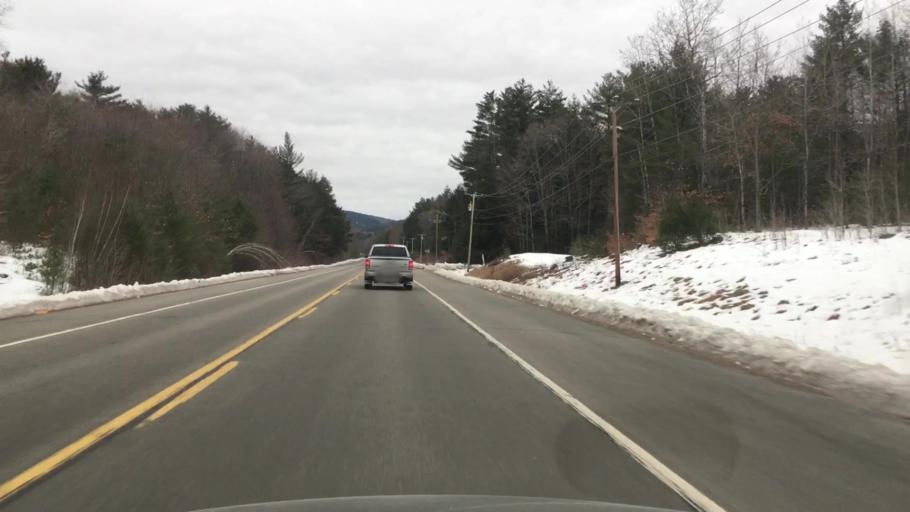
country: US
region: New Hampshire
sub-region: Merrimack County
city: Newbury
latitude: 43.2972
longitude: -71.9970
